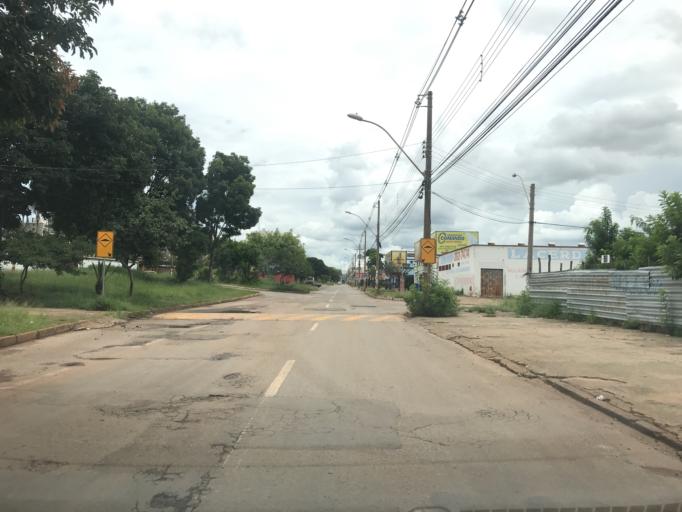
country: BR
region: Federal District
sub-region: Brasilia
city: Brasilia
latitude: -15.8193
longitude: -47.9558
